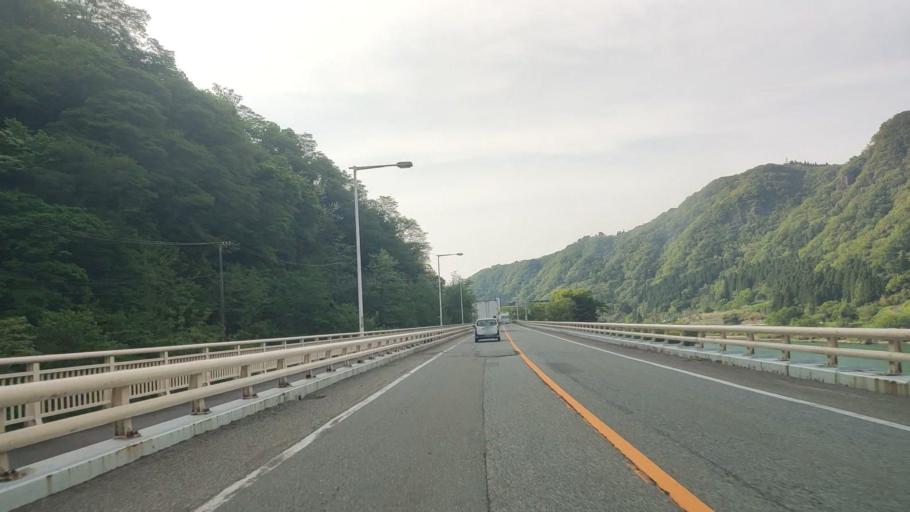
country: JP
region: Toyama
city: Yatsuomachi-higashikumisaka
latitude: 36.5443
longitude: 137.2283
